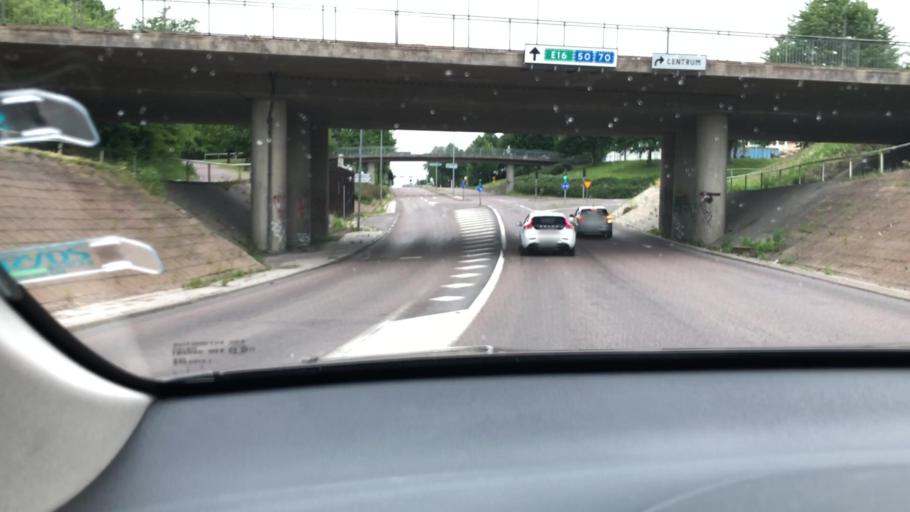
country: SE
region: Dalarna
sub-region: Borlange Kommun
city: Borlaenge
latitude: 60.4898
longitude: 15.4343
